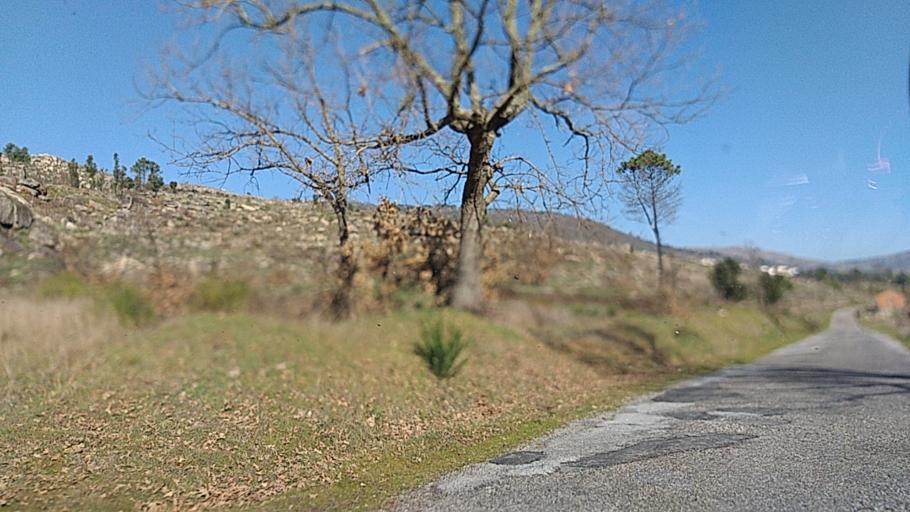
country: PT
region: Guarda
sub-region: Celorico da Beira
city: Celorico da Beira
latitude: 40.6724
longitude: -7.4566
